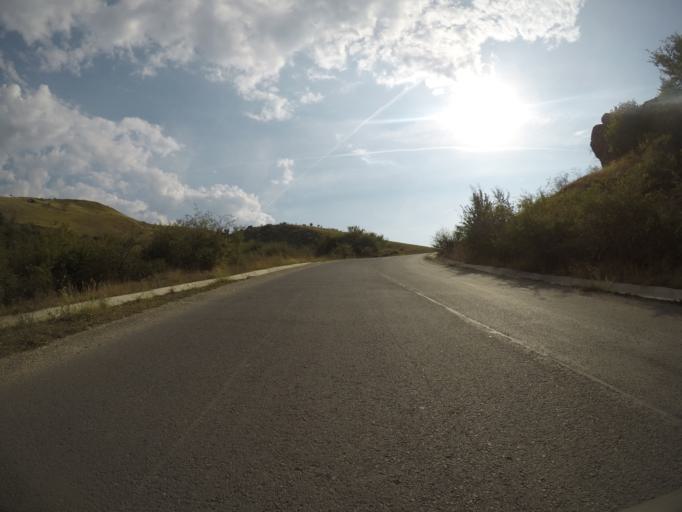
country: RO
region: Cluj
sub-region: Comuna Sandulesti
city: Sandulesti
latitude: 46.5589
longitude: 23.6940
